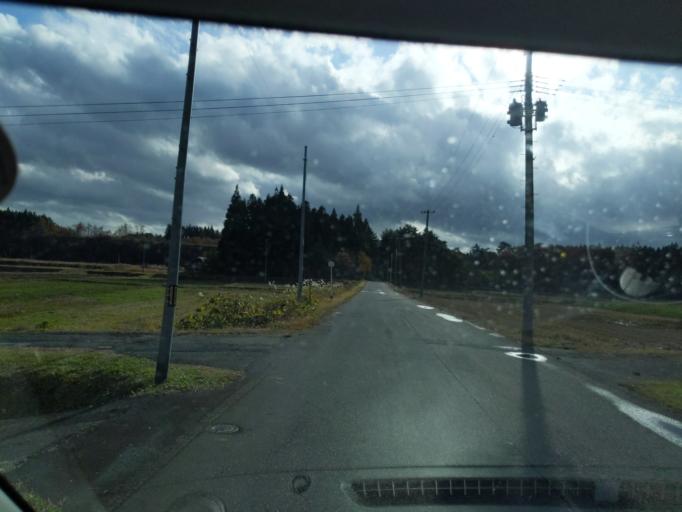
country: JP
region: Iwate
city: Mizusawa
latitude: 39.1080
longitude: 140.9720
